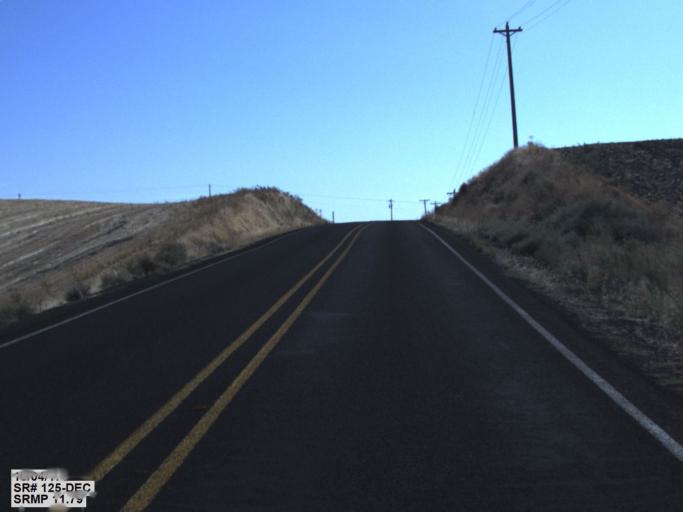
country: US
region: Washington
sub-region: Walla Walla County
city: Walla Walla
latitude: 46.1424
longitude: -118.3726
